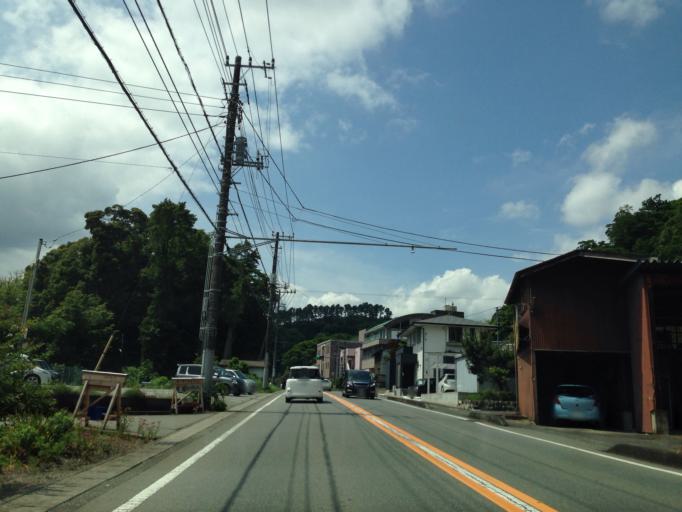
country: JP
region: Shizuoka
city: Heda
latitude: 34.9442
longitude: 138.9316
